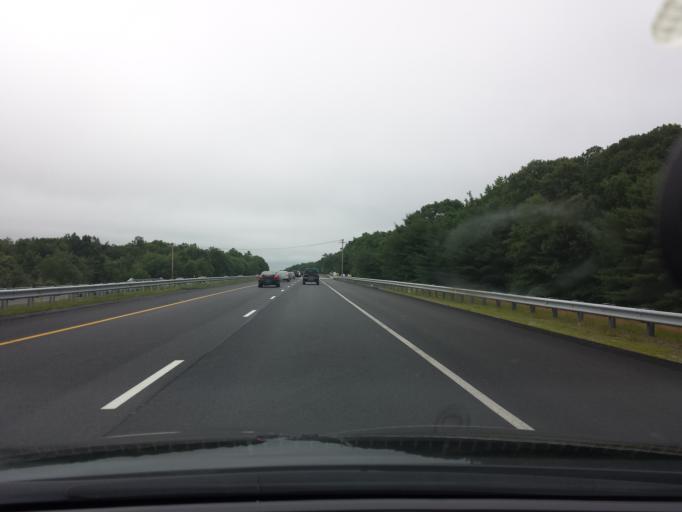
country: US
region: Rhode Island
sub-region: Kent County
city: West Greenwich
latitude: 41.5768
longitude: -71.6607
